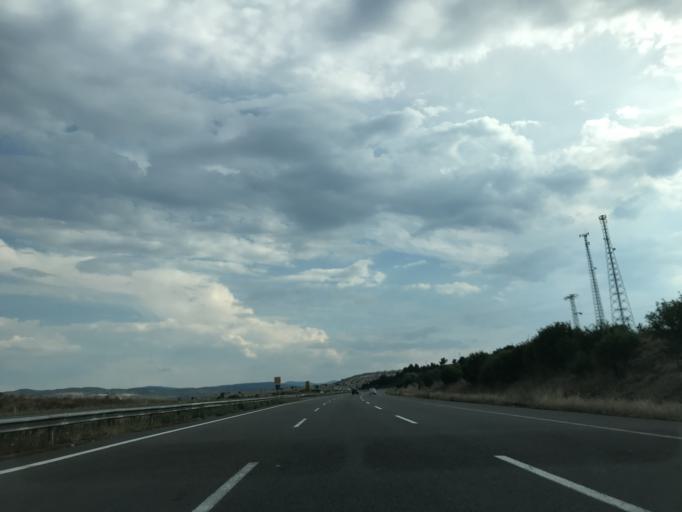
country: TR
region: Bolu
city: Gerede
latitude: 40.6898
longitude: 32.2227
